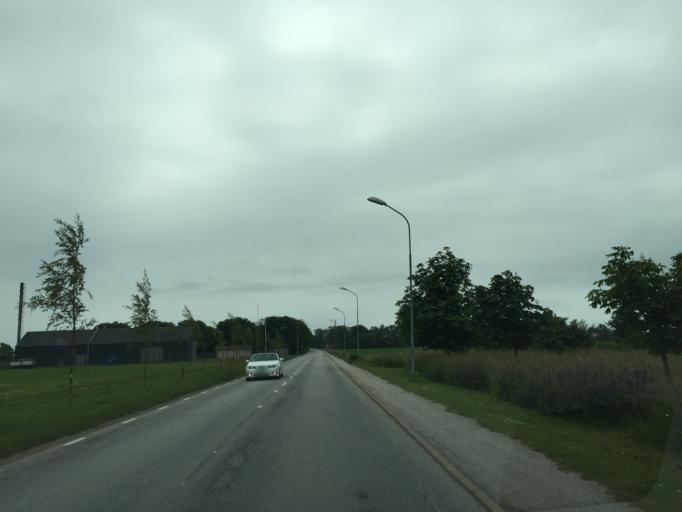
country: SE
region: Skane
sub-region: Ystads Kommun
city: Kopingebro
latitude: 55.4329
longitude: 14.1133
